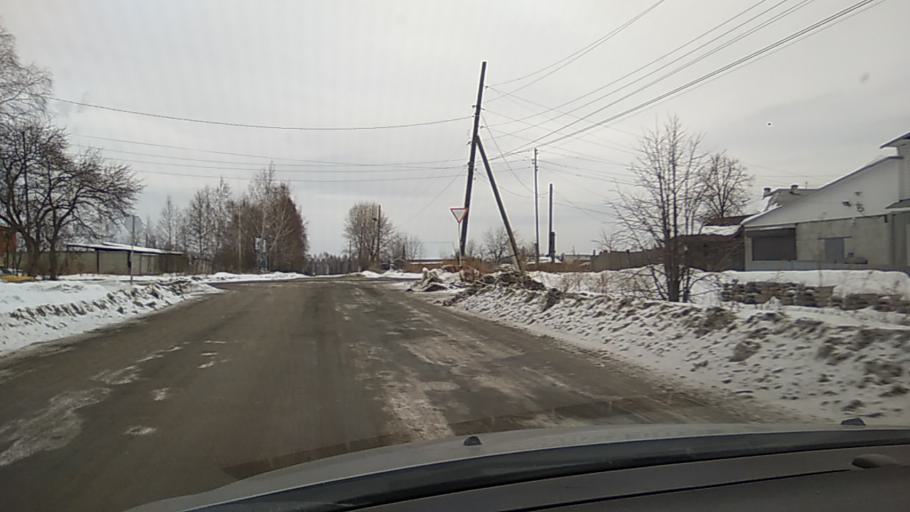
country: RU
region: Sverdlovsk
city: Revda
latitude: 56.8102
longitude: 59.9359
